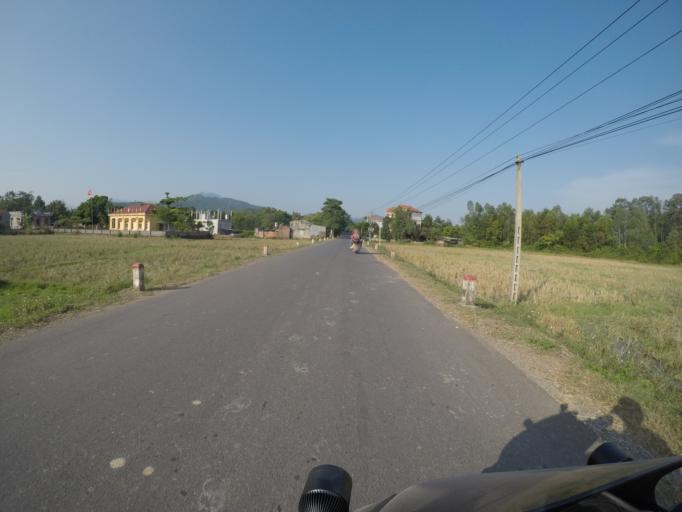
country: VN
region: Vinh Phuc
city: Huong Canh
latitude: 21.3523
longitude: 105.7072
